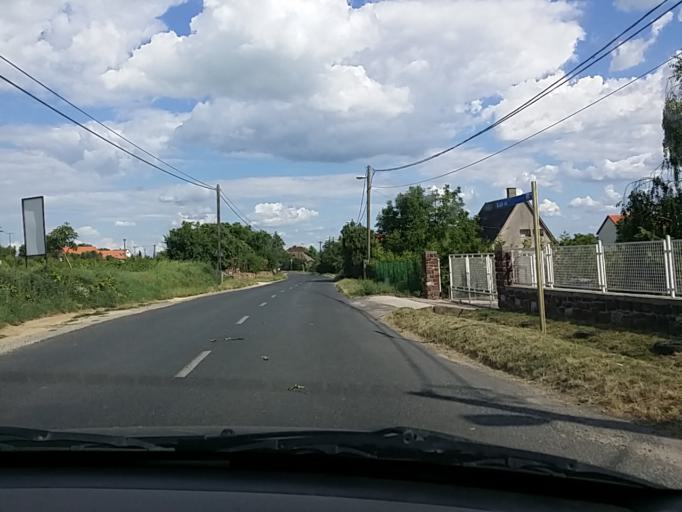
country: HU
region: Veszprem
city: Revfueloep
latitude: 46.8309
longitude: 17.6154
